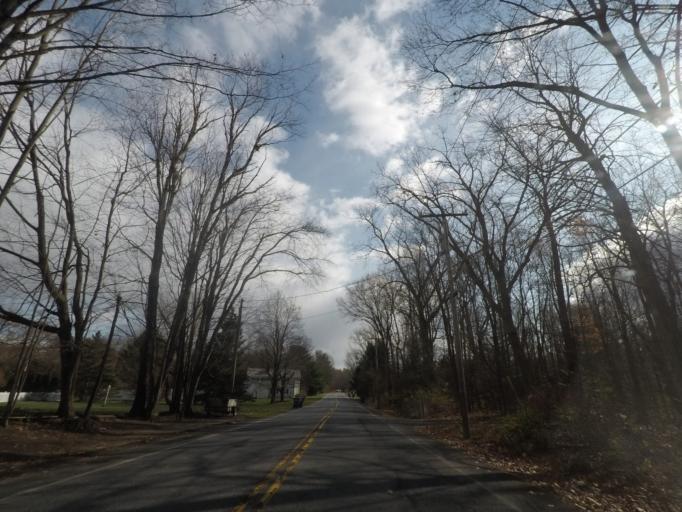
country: US
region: New York
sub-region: Saratoga County
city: Country Knolls
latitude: 42.8946
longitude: -73.8133
